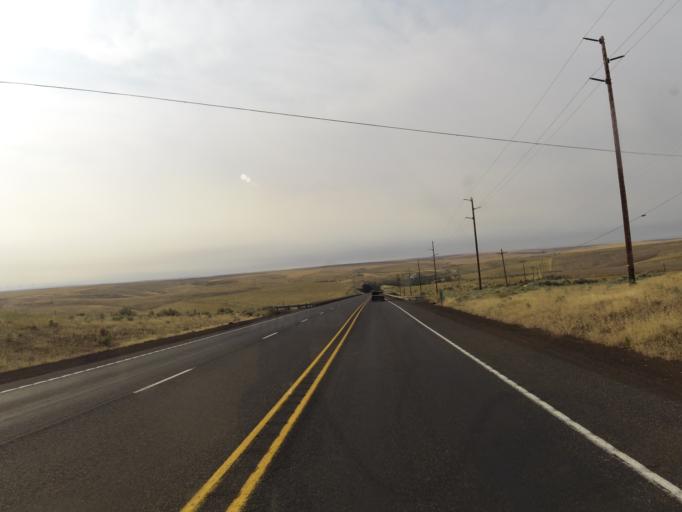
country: US
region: Oregon
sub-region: Sherman County
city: Moro
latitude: 45.5233
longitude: -120.6882
